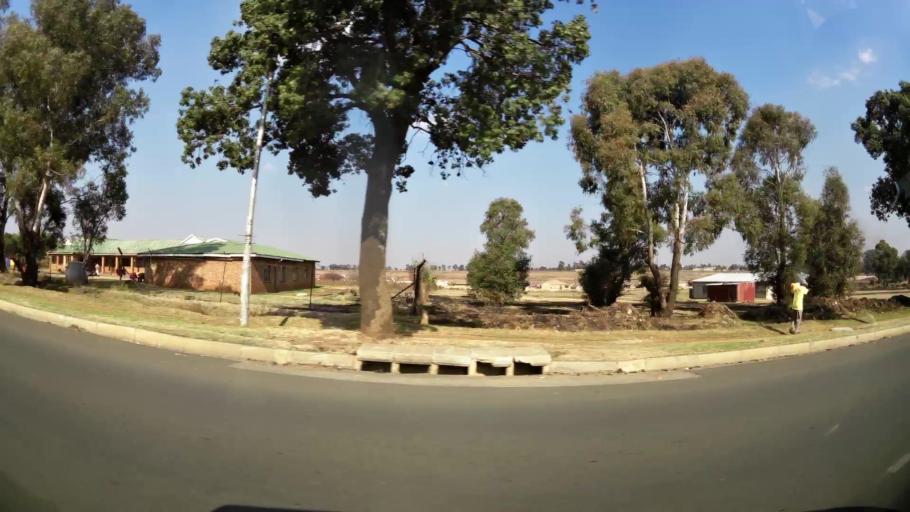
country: ZA
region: Gauteng
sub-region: Ekurhuleni Metropolitan Municipality
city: Brakpan
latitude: -26.1607
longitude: 28.4077
